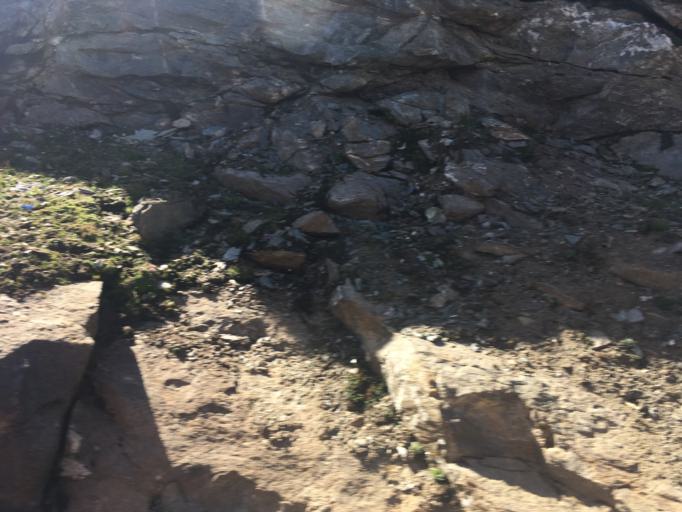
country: CH
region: Valais
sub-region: Visp District
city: Zermatt
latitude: 45.9867
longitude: 7.7591
